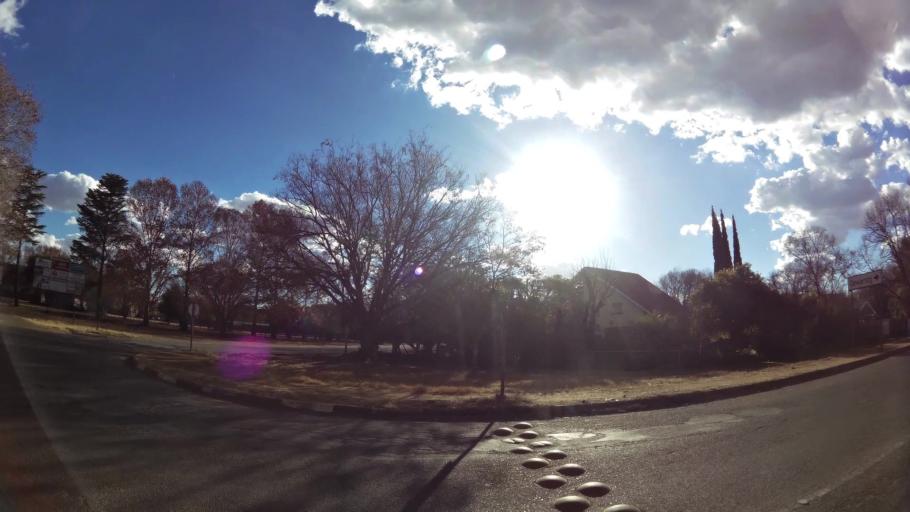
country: ZA
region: North-West
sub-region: Dr Kenneth Kaunda District Municipality
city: Potchefstroom
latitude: -26.6858
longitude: 27.0999
